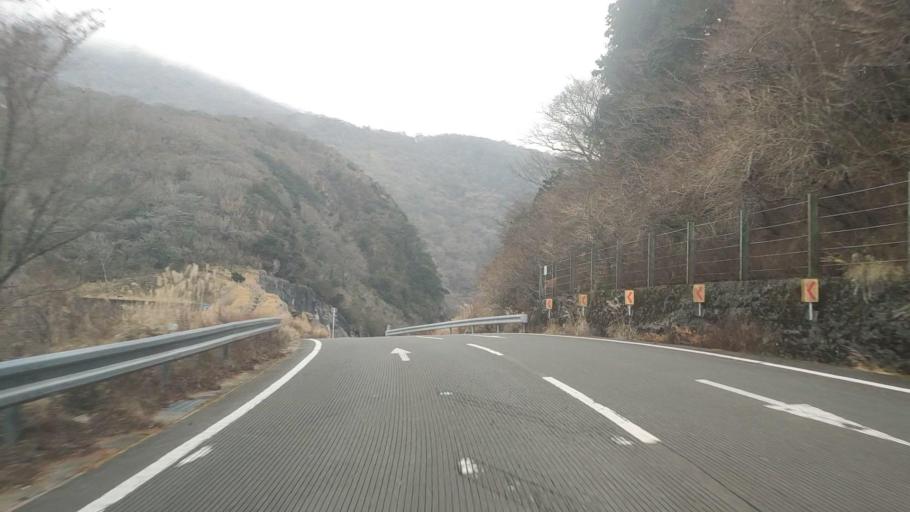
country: JP
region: Nagasaki
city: Shimabara
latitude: 32.7636
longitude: 130.2745
